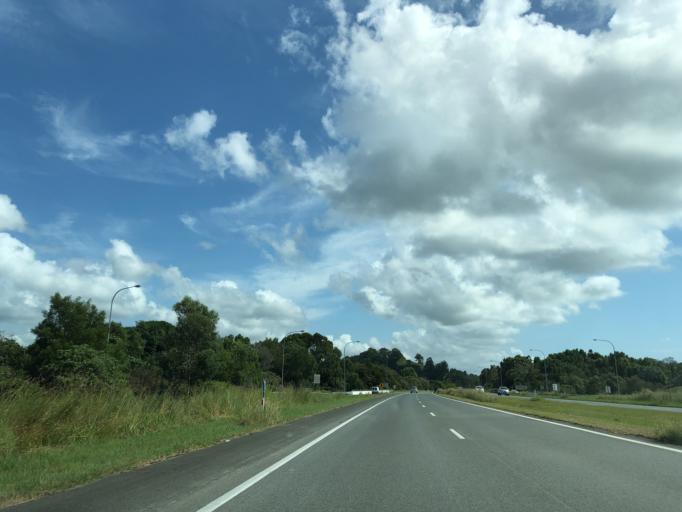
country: AU
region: New South Wales
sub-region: Tweed
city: Pottsville Beach
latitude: -28.3891
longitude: 153.5239
